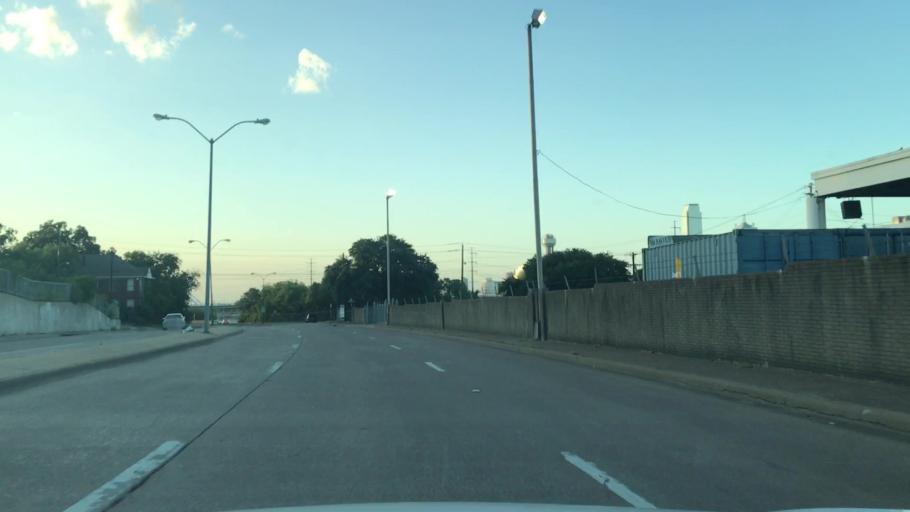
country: US
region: Texas
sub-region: Dallas County
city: Dallas
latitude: 32.7562
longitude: -96.8109
